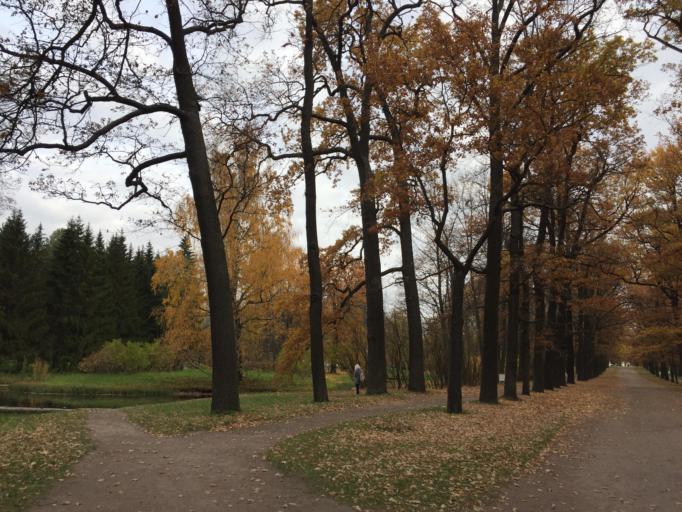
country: RU
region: St.-Petersburg
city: Pushkin
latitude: 59.7112
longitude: 30.3873
